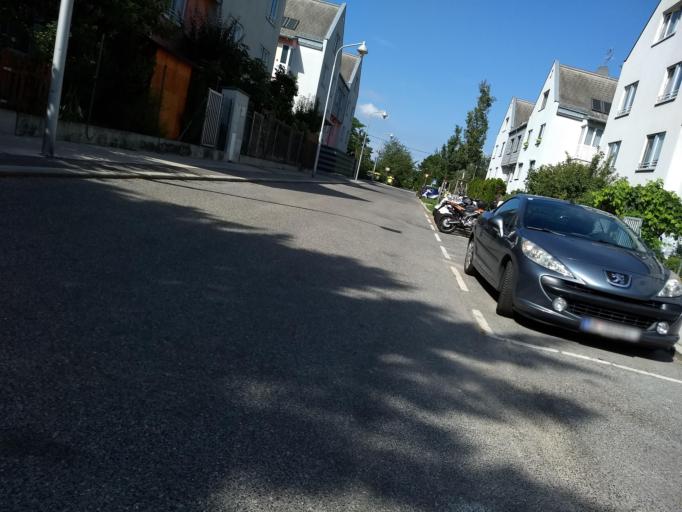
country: AT
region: Lower Austria
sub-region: Politischer Bezirk Ganserndorf
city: Gross-Enzersdorf
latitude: 48.2321
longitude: 16.4935
